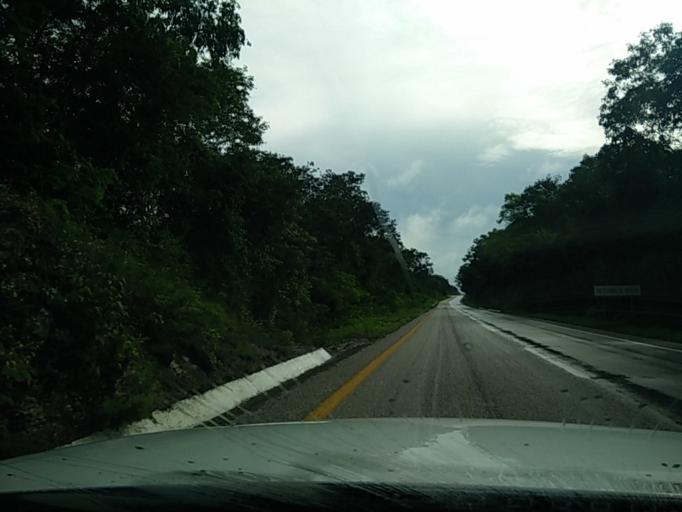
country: MX
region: Yucatan
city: Tunkas
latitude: 20.7557
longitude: -88.7479
